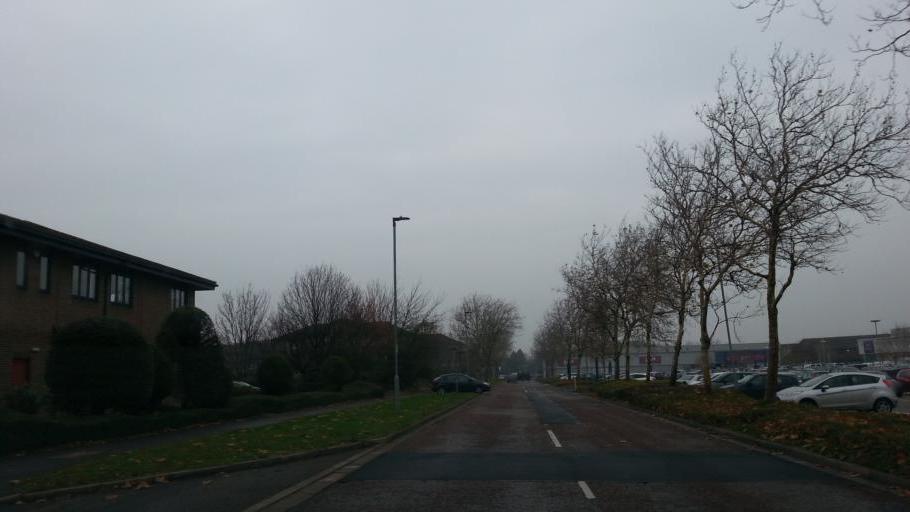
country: GB
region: England
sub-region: Cambridgeshire
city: Yaxley
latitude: 52.5421
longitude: -0.3035
